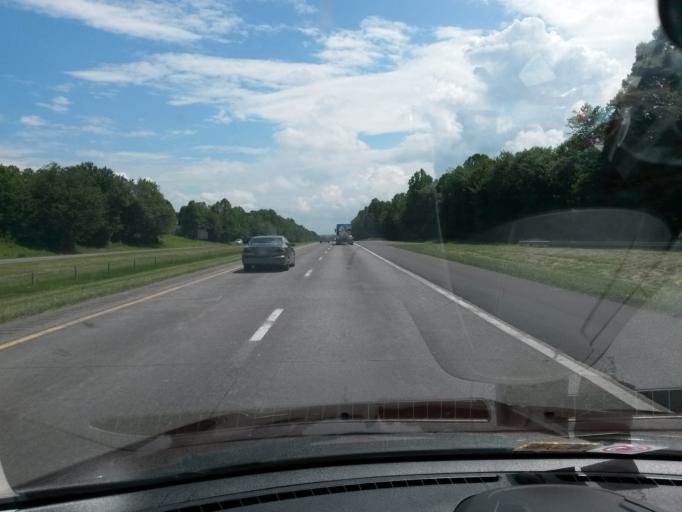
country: US
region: North Carolina
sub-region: Surry County
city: Dobson
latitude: 36.3908
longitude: -80.7884
